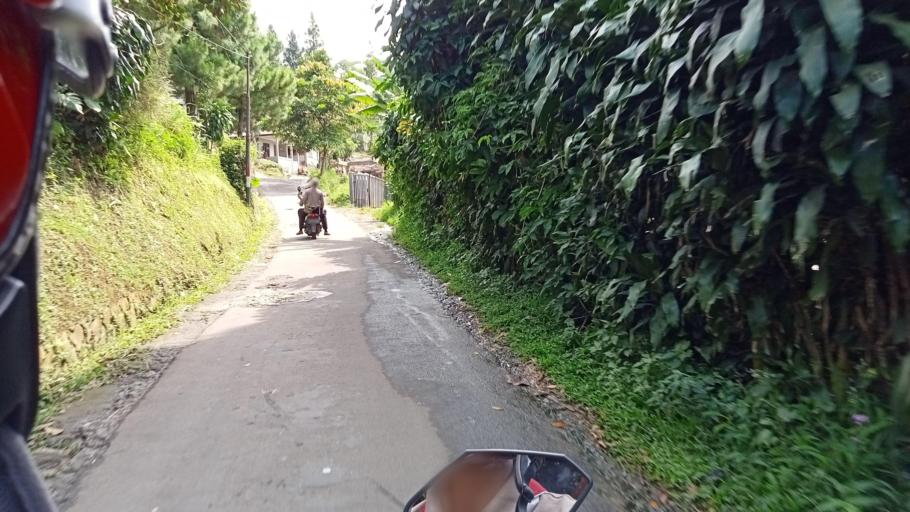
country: ID
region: West Java
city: Caringin
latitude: -6.6438
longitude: 106.9073
